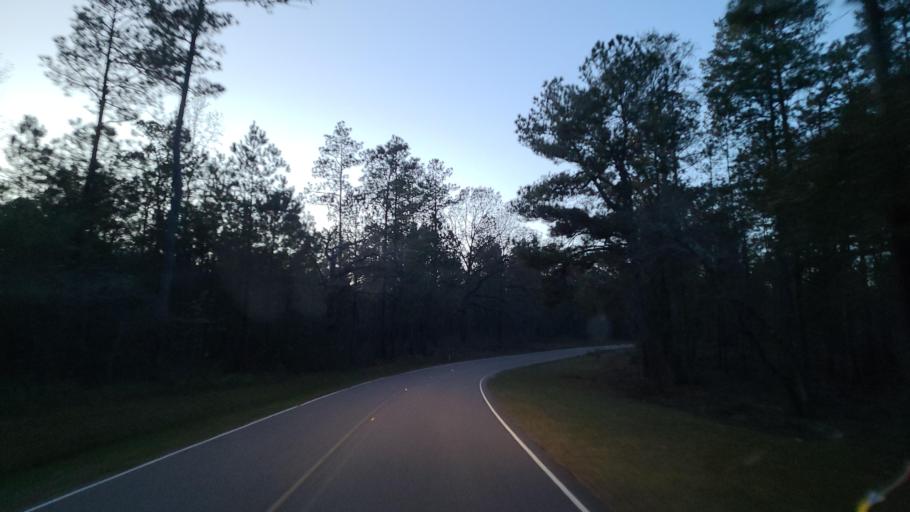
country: US
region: Mississippi
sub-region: Forrest County
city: Hattiesburg
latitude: 31.1867
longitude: -89.2346
